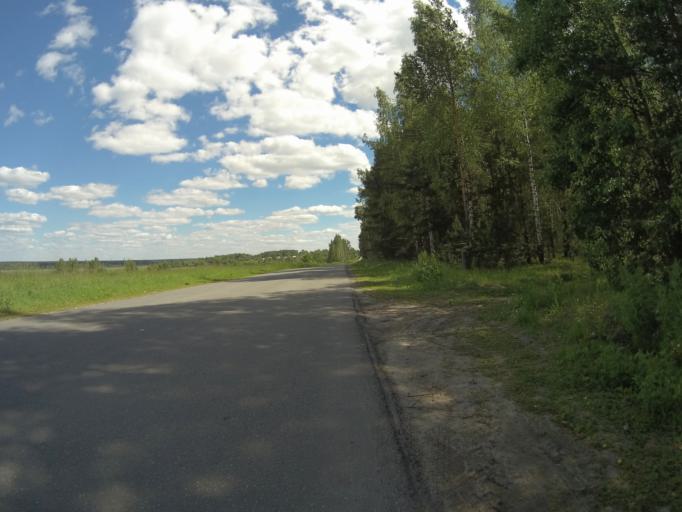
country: RU
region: Vladimir
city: Sudogda
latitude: 56.0662
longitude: 40.8033
